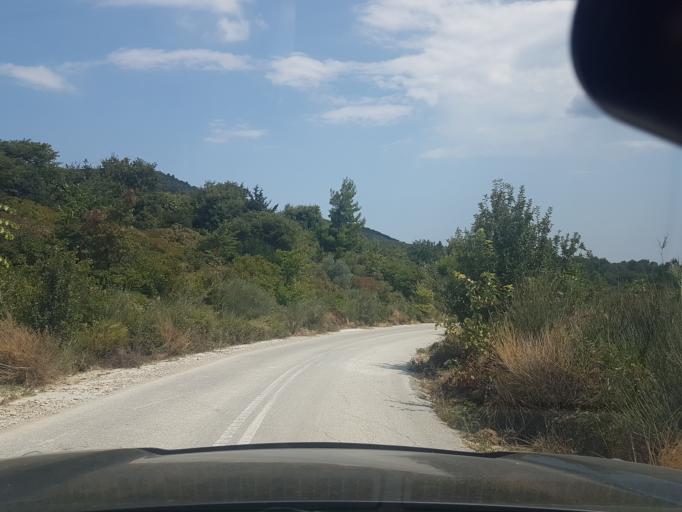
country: GR
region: Central Greece
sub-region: Nomos Evvoias
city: Kymi
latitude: 38.6476
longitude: 24.0461
